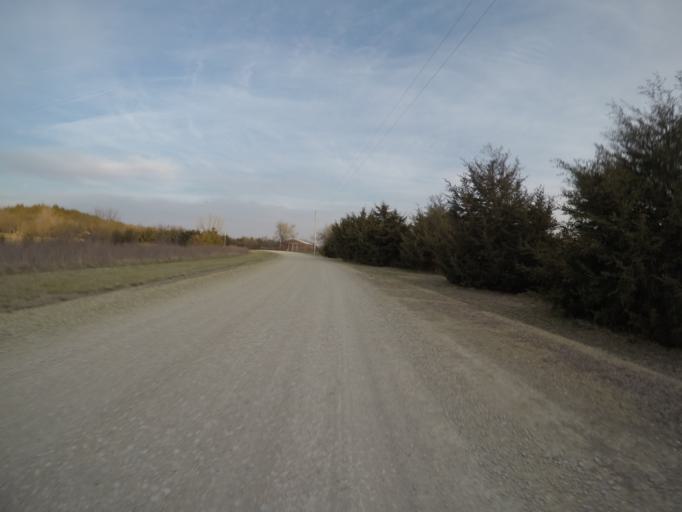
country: US
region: Kansas
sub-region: Riley County
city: Ogden
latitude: 39.1742
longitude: -96.6768
